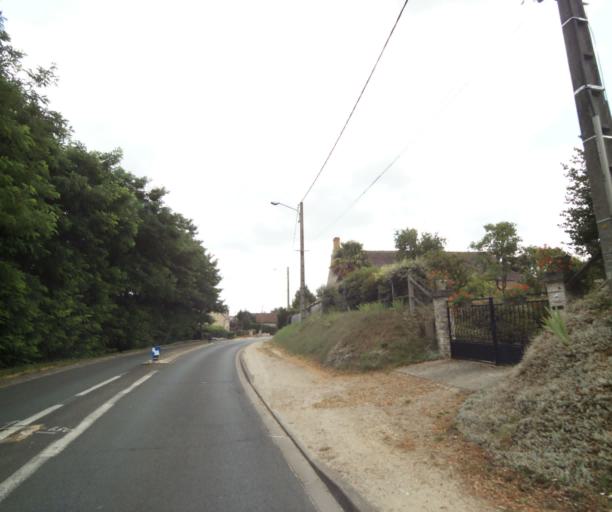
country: FR
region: Centre
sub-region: Departement du Loiret
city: Saint-Cyr-en-Val
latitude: 47.8401
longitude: 1.9531
